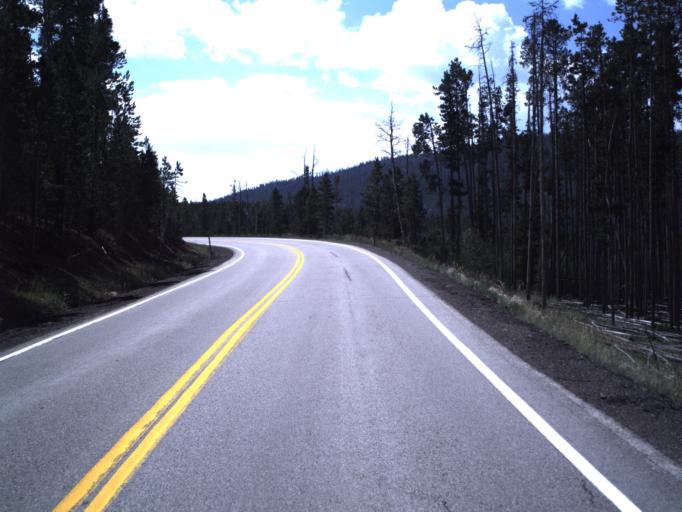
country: US
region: Utah
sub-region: Uintah County
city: Maeser
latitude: 40.7602
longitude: -109.4707
